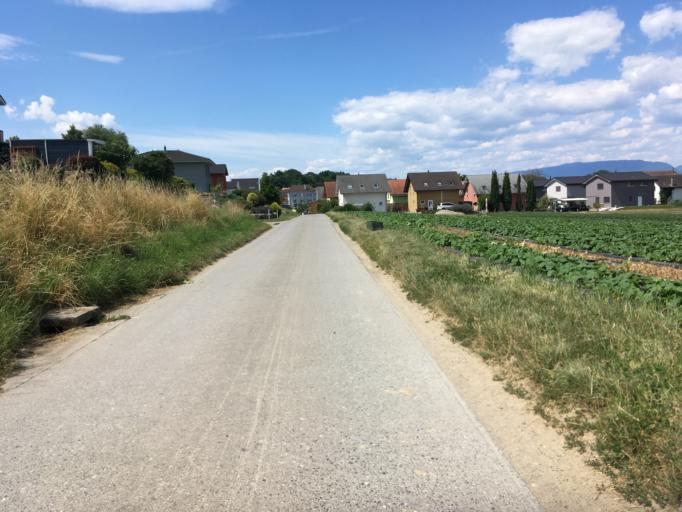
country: CH
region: Neuchatel
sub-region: Neuchatel District
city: Saint-Blaise
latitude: 46.9540
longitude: 7.0255
